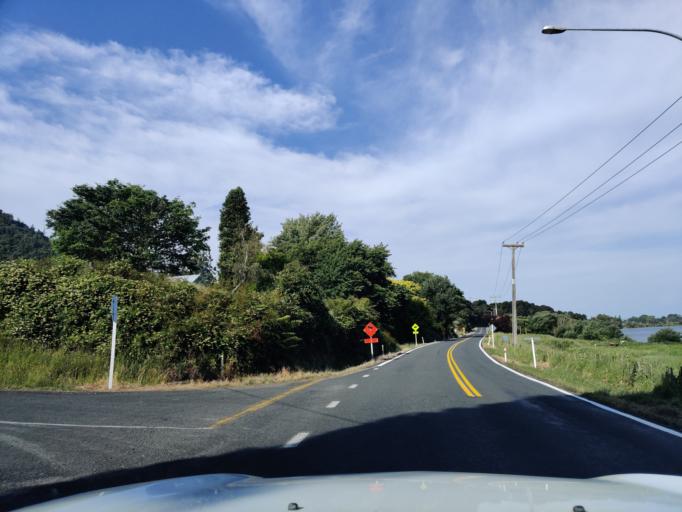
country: NZ
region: Waikato
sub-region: Waikato District
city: Ngaruawahia
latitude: -37.6337
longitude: 175.1533
